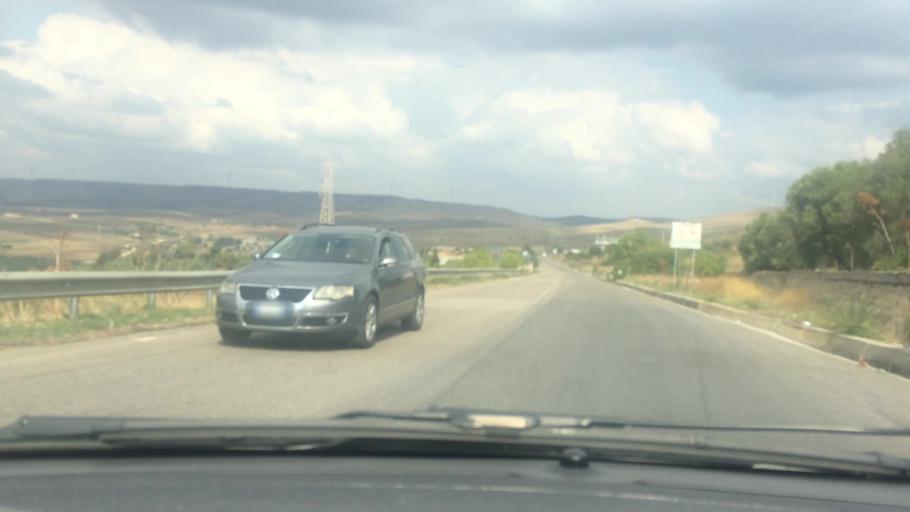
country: IT
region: Basilicate
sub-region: Provincia di Matera
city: Matera
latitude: 40.6818
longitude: 16.5715
